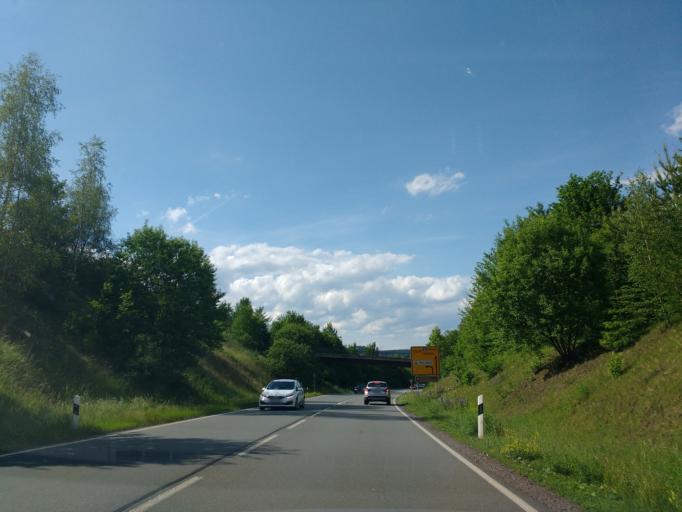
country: DE
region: Hesse
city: Frankenberg
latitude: 51.0682
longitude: 8.8142
